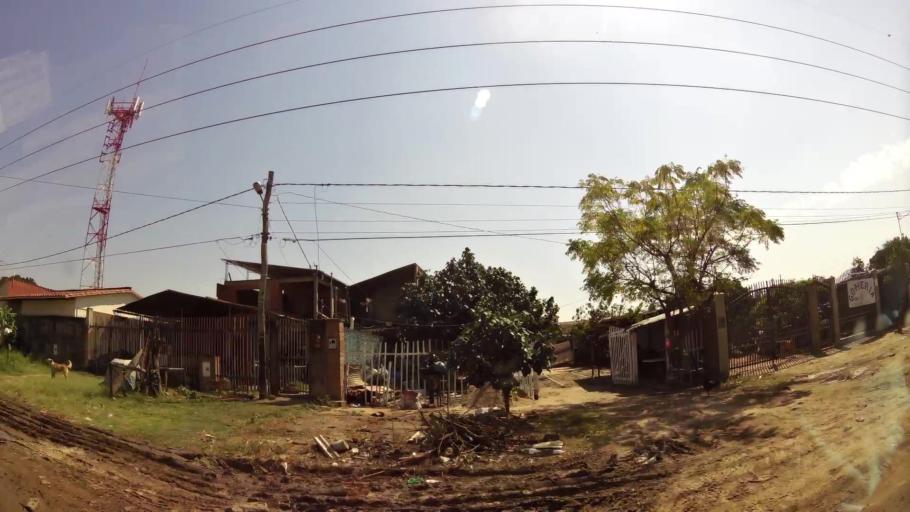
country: BO
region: Santa Cruz
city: Santa Cruz de la Sierra
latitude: -17.7287
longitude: -63.1590
